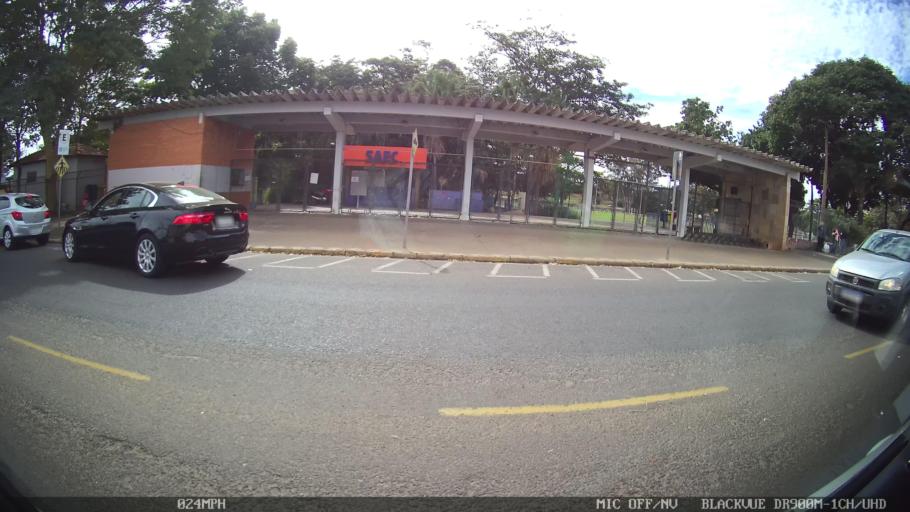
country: BR
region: Sao Paulo
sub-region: Catanduva
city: Catanduva
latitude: -21.1406
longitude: -48.9640
